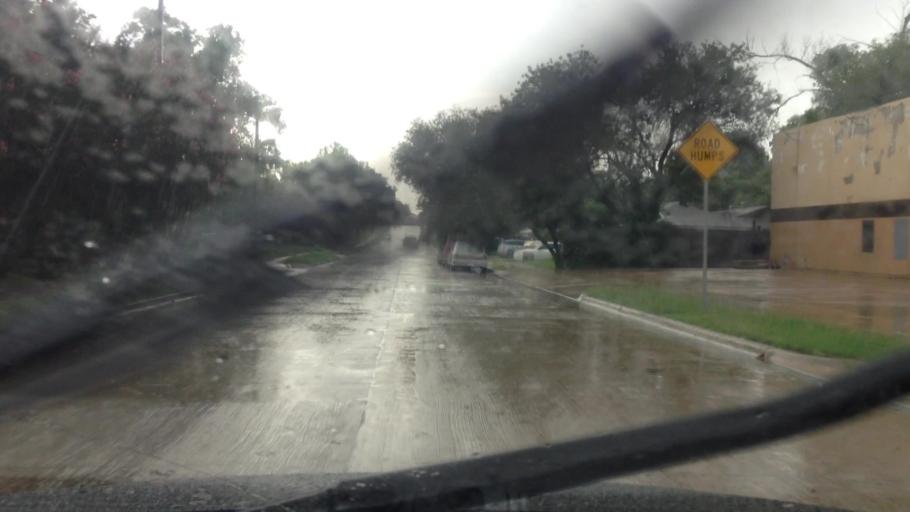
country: US
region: Texas
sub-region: Tarrant County
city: North Richland Hills
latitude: 32.8392
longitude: -97.2079
